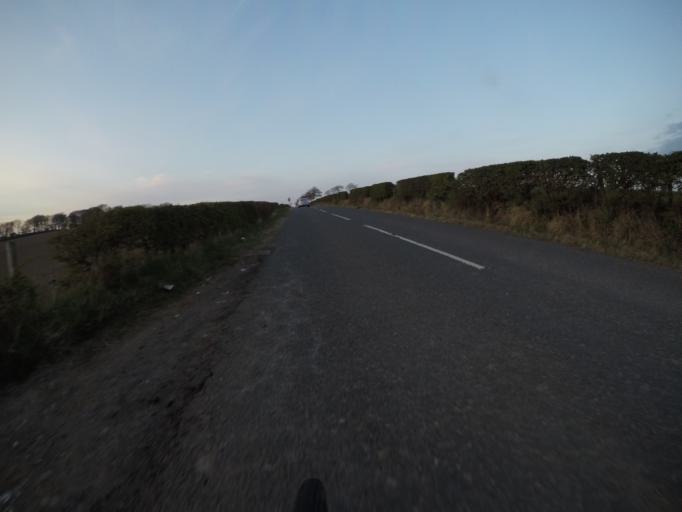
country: GB
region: Scotland
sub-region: South Ayrshire
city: Dundonald
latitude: 55.5601
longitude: -4.6093
